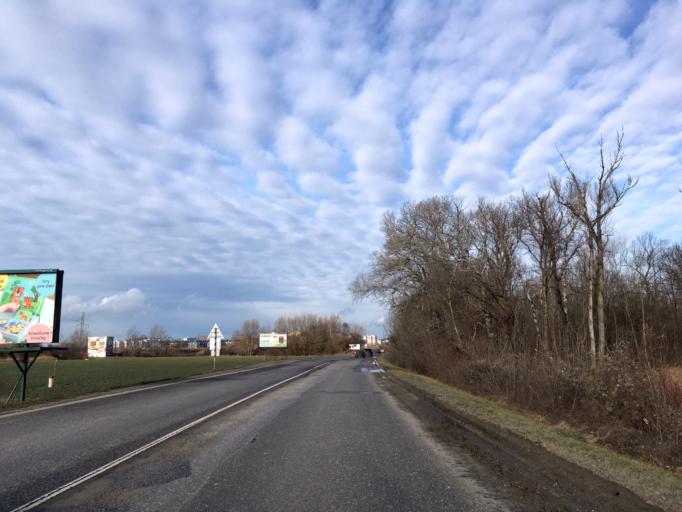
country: AT
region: Burgenland
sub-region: Politischer Bezirk Neusiedl am See
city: Kittsee
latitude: 48.0818
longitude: 17.1260
